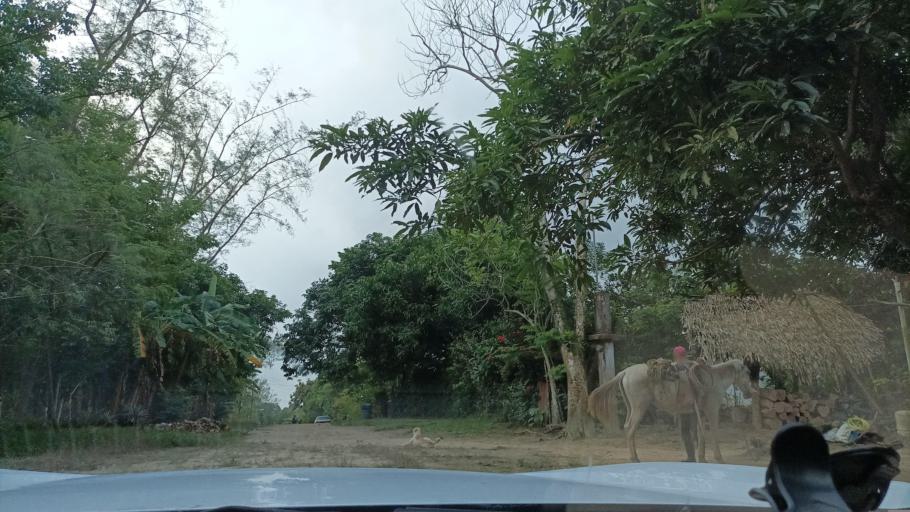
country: MX
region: Veracruz
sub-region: Moloacan
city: Cuichapa
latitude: 17.9244
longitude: -94.3661
